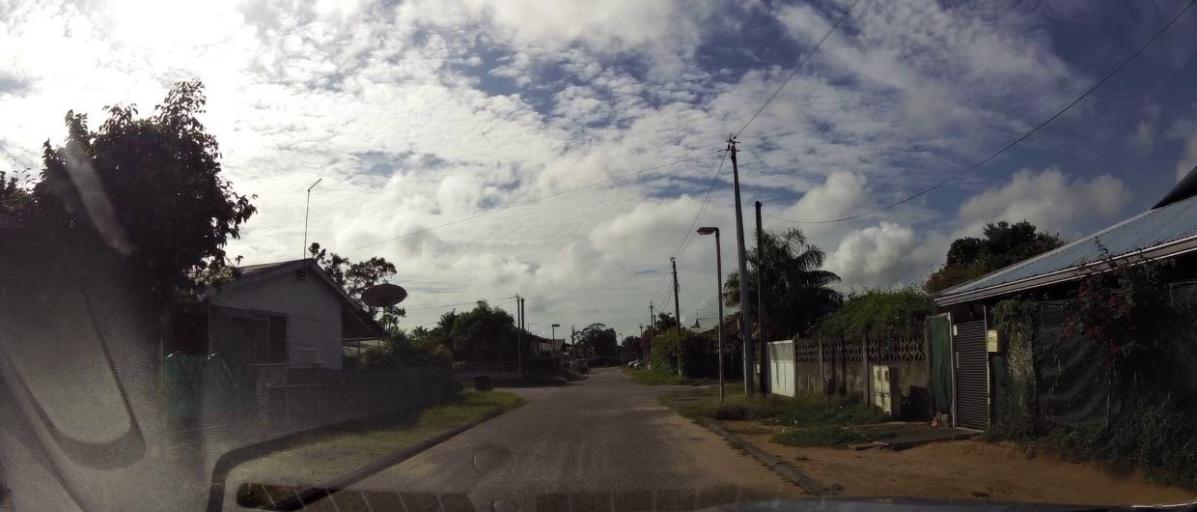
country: GF
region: Guyane
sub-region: Guyane
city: Kourou
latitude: 5.1604
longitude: -52.6418
